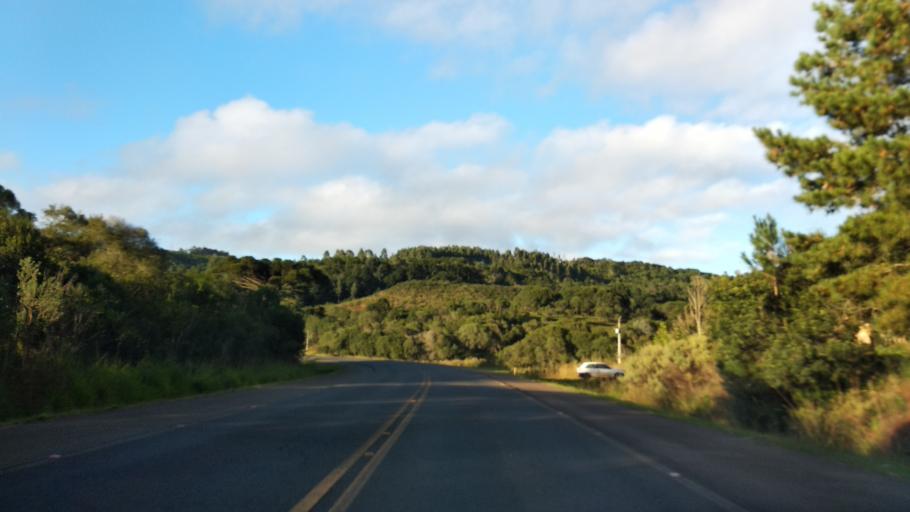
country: BR
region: Santa Catarina
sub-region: Curitibanos
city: Curitibanos
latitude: -27.5919
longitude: -50.7358
